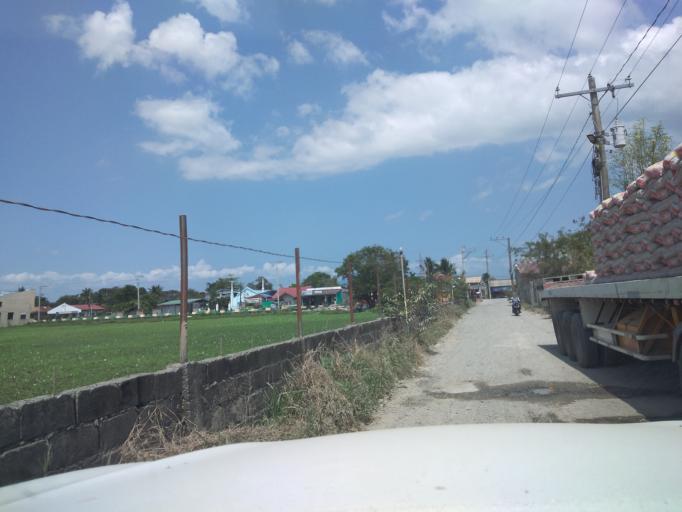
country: PH
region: Central Luzon
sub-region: Province of Pampanga
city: Lourdes
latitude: 15.0181
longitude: 120.8573
